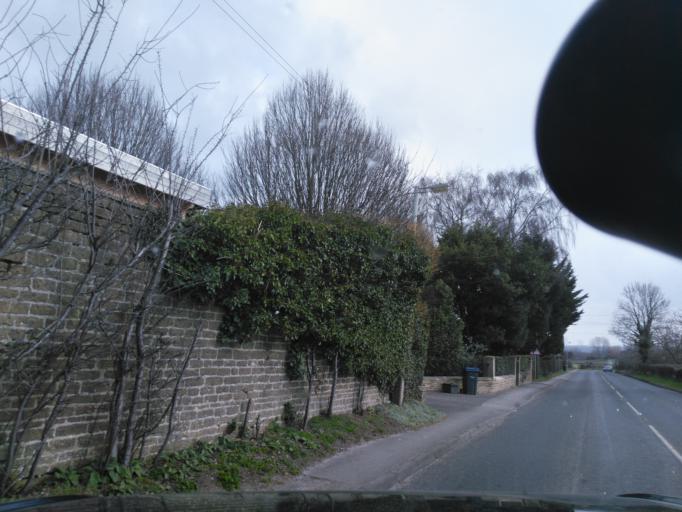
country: GB
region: England
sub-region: Wiltshire
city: Atworth
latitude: 51.3911
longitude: -2.1769
